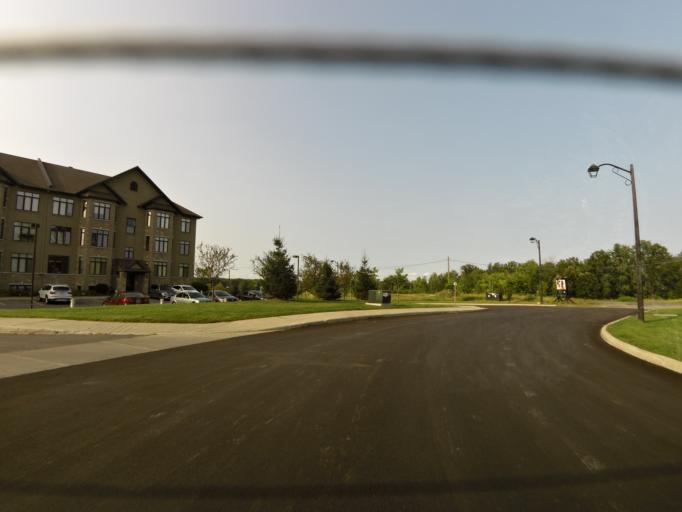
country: CA
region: Quebec
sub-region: Outaouais
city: Gatineau
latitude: 45.4913
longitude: -75.4958
